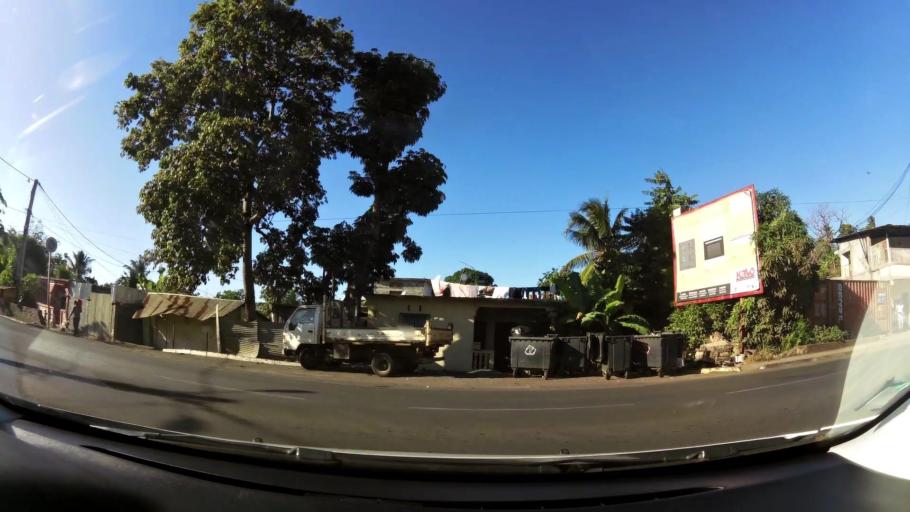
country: YT
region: Mamoudzou
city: Mamoudzou
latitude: -12.7538
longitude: 45.2318
